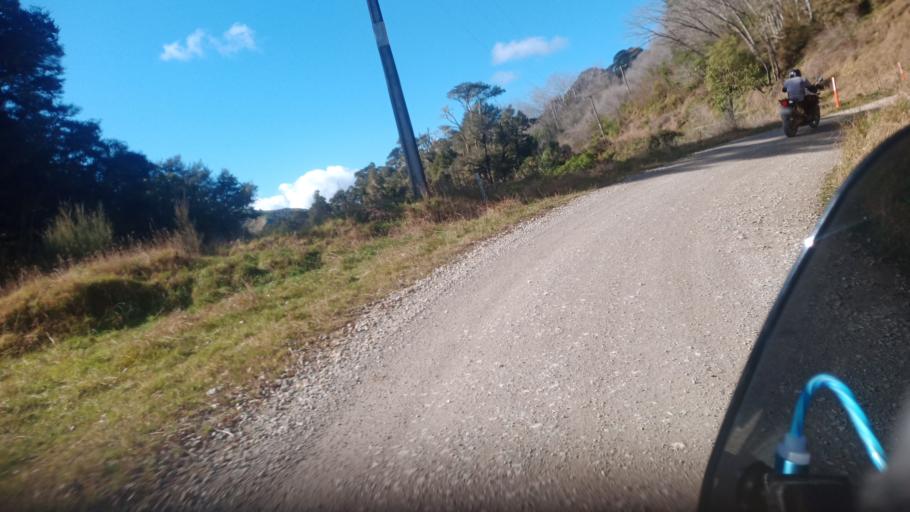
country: NZ
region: Hawke's Bay
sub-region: Wairoa District
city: Wairoa
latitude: -38.6635
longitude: 177.5108
